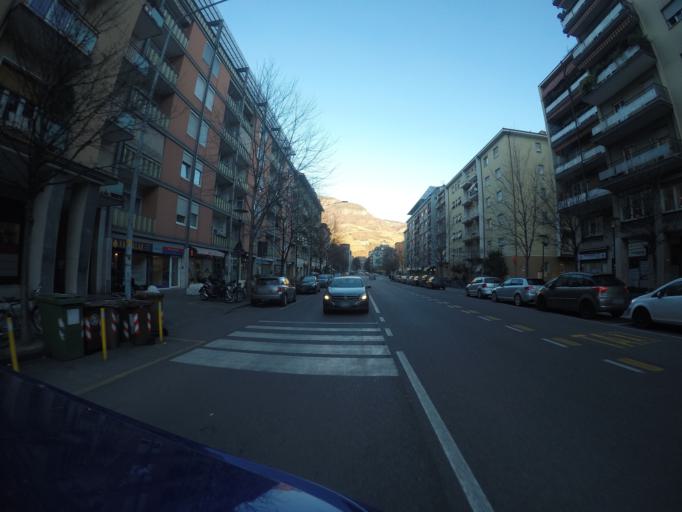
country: IT
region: Trentino-Alto Adige
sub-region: Bolzano
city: Bolzano
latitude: 46.4908
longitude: 11.3419
